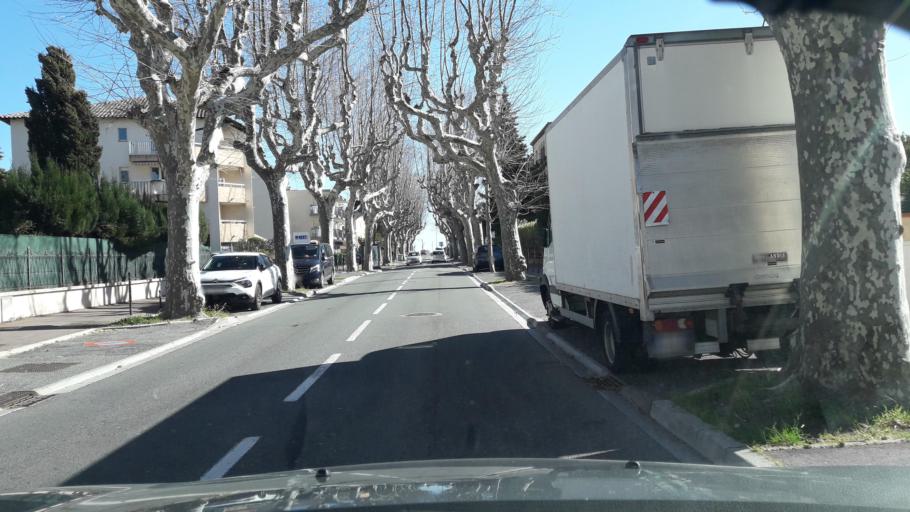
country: FR
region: Provence-Alpes-Cote d'Azur
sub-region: Departement du Var
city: Frejus
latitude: 43.4211
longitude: 6.7438
